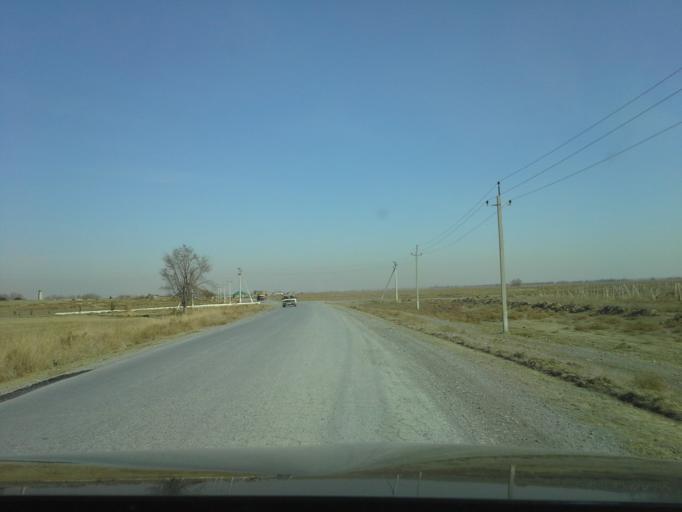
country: TM
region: Ahal
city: Abadan
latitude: 38.1113
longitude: 57.9880
